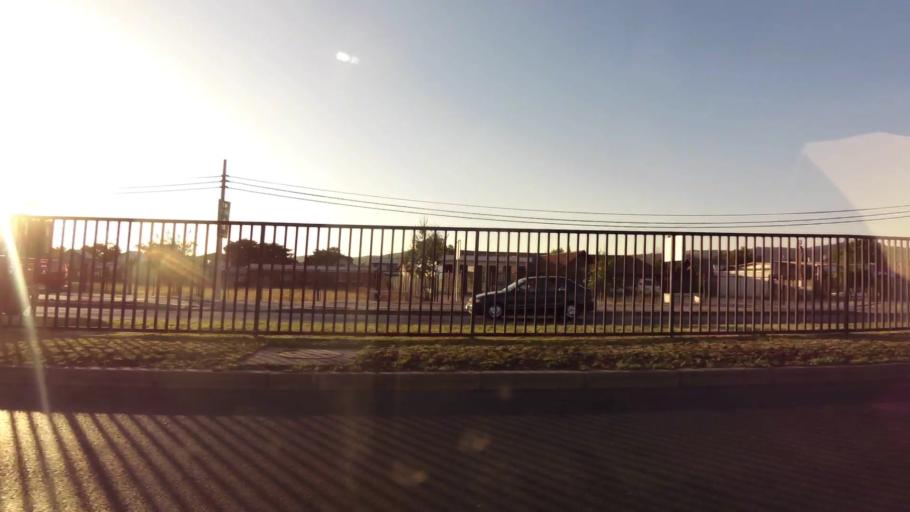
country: CL
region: Maule
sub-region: Provincia de Talca
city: Talca
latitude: -35.4473
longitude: -71.6892
